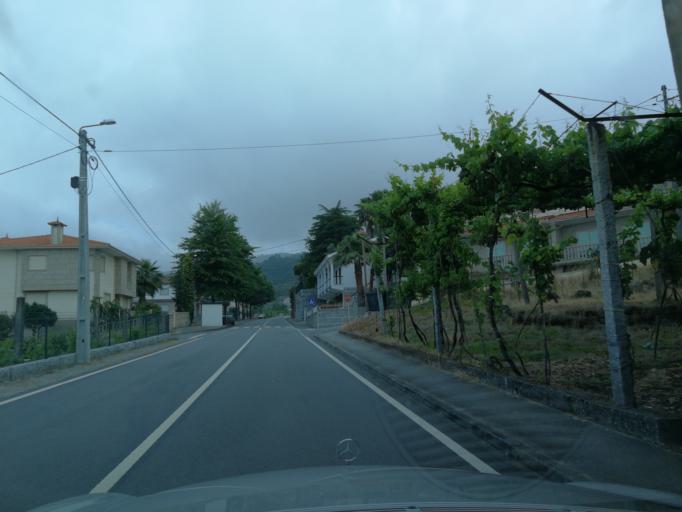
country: PT
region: Braga
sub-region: Guimaraes
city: Ponte
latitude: 41.5148
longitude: -8.3563
